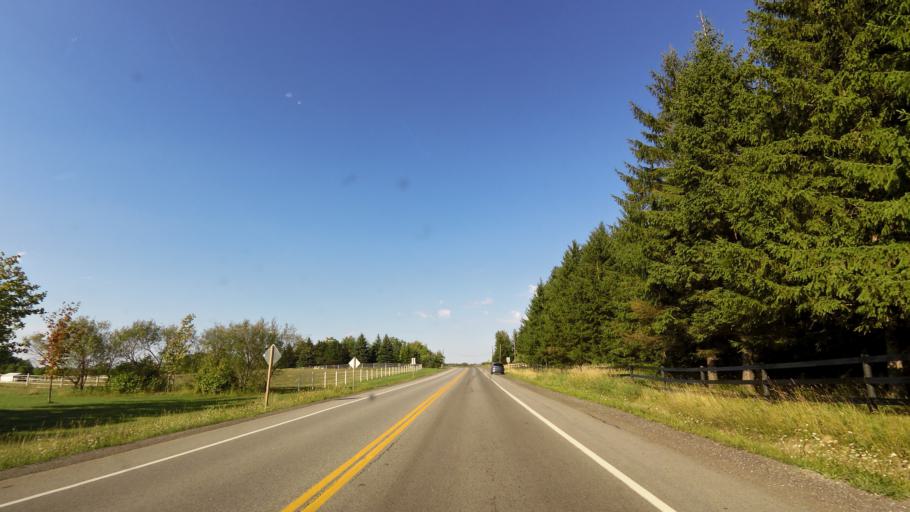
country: CA
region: Ontario
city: Brampton
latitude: 43.7375
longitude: -79.9173
